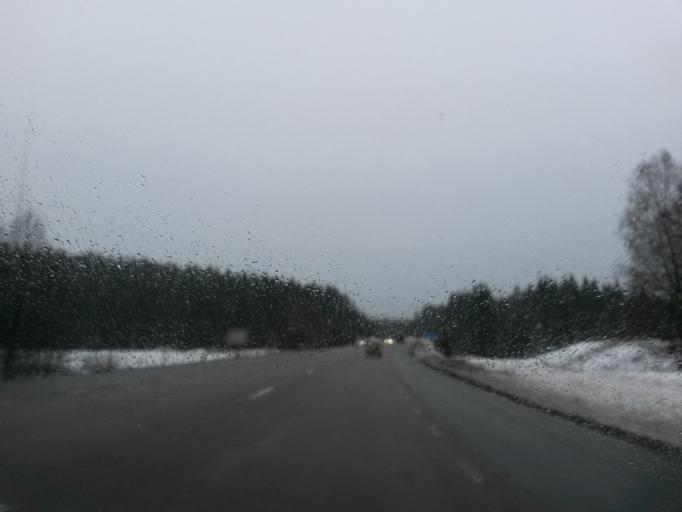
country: SE
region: Vaestra Goetaland
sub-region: Boras Kommun
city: Boras
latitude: 57.6597
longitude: 12.9184
